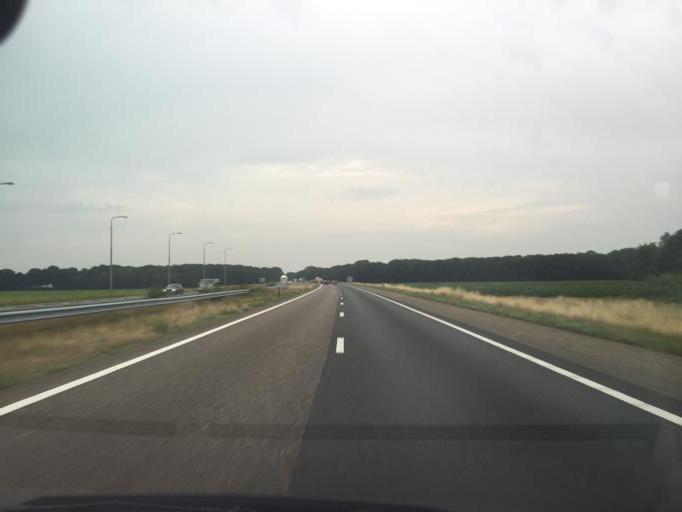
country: NL
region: Limburg
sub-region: Gemeente Leudal
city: Heythuysen
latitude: 51.3787
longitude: 5.9101
